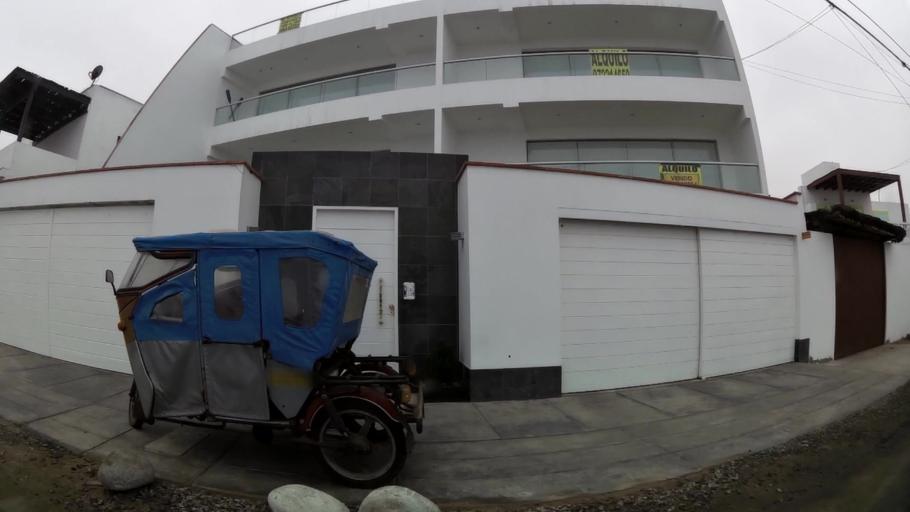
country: PE
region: Lima
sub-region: Lima
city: Punta Hermosa
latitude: -12.3352
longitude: -76.8283
